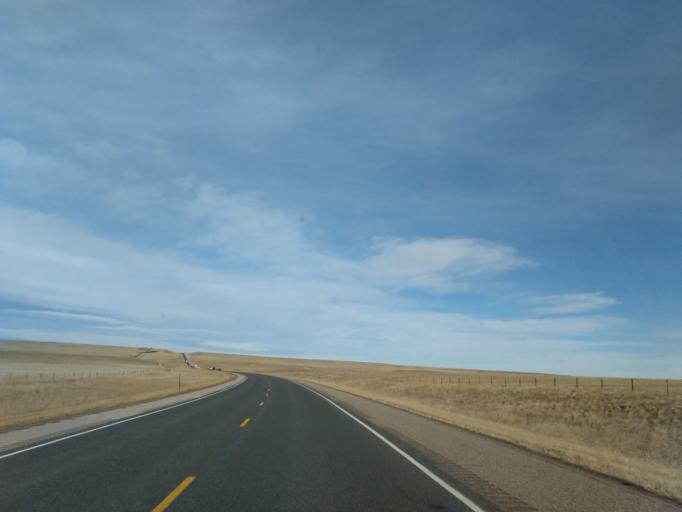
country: US
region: Wyoming
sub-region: Laramie County
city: Pine Bluffs
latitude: 41.5759
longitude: -104.2741
